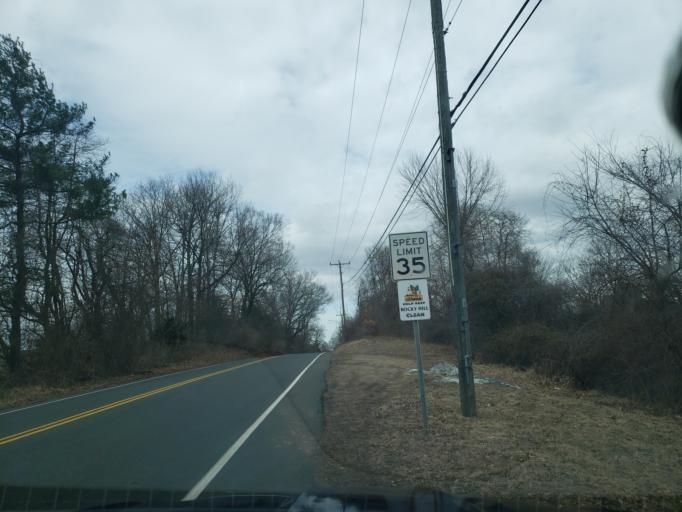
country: US
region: Connecticut
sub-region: Middlesex County
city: Cromwell
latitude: 41.6524
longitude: -72.6630
